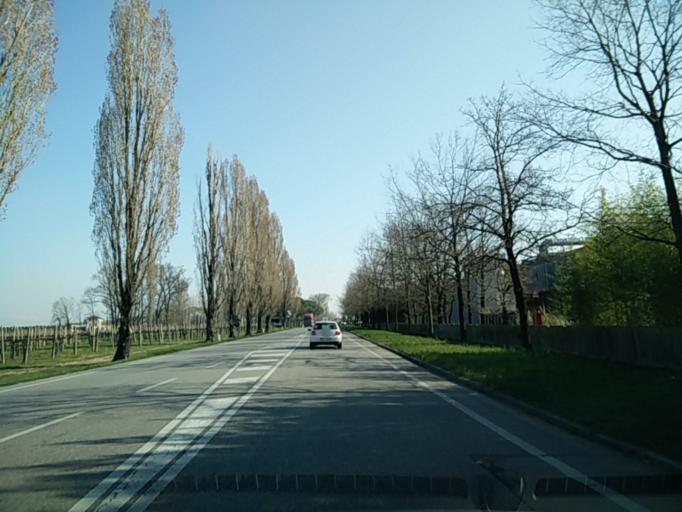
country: IT
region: Friuli Venezia Giulia
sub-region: Provincia di Pordenone
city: Villotta
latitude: 45.8694
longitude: 12.7688
